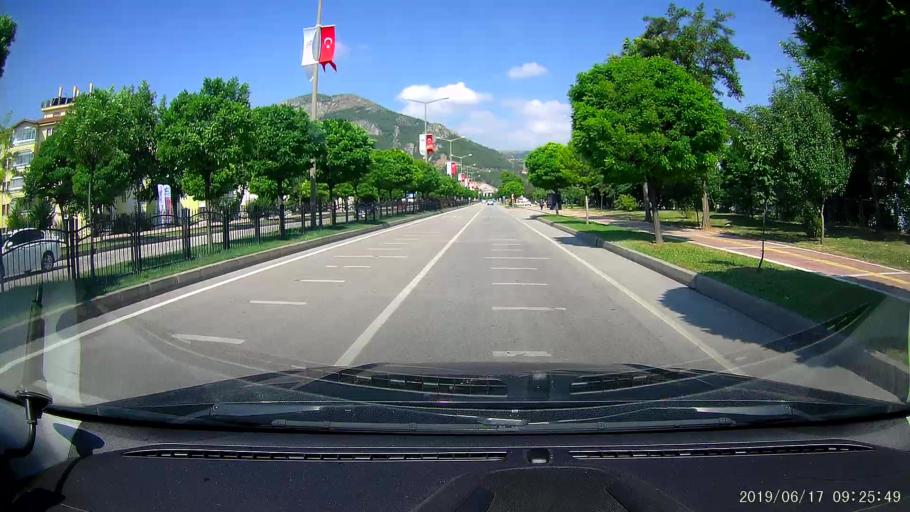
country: TR
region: Amasya
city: Amasya
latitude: 40.6682
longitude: 35.8436
